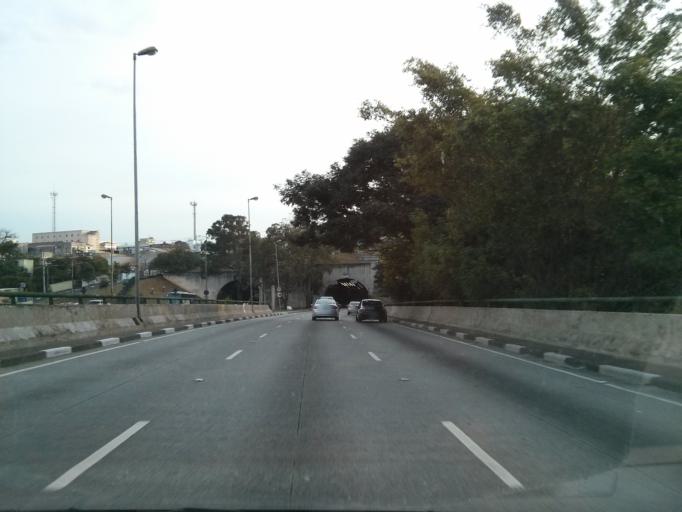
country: BR
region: Sao Paulo
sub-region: Diadema
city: Diadema
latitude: -23.6258
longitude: -46.6157
